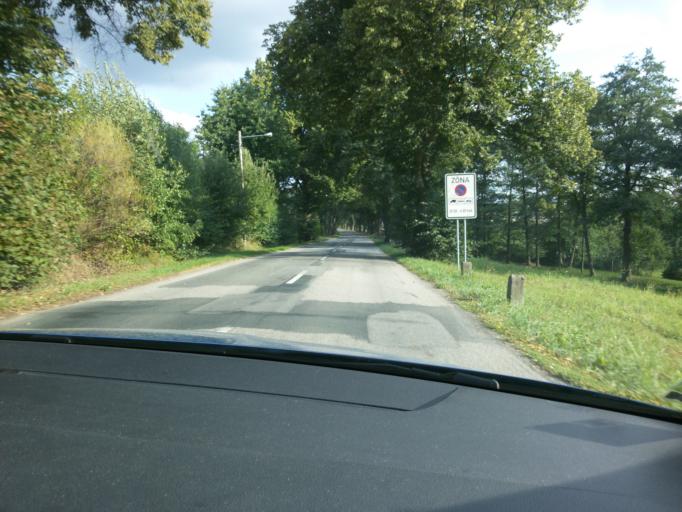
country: CZ
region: South Moravian
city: Olesnice
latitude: 49.5634
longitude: 16.4156
